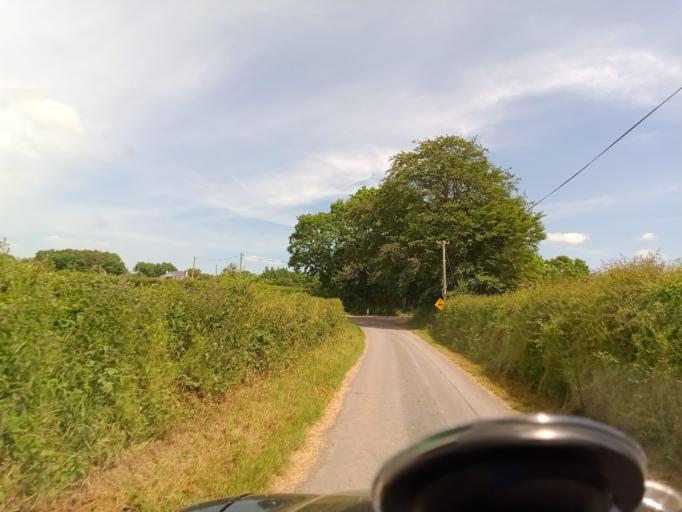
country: IE
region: Leinster
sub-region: Kilkenny
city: Thomastown
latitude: 52.5649
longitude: -7.0969
